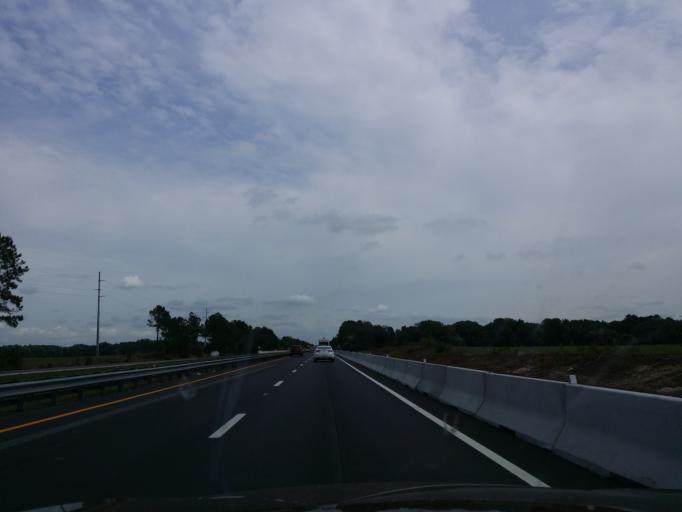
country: US
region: Florida
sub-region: Sumter County
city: Bushnell
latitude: 28.6856
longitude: -82.1330
